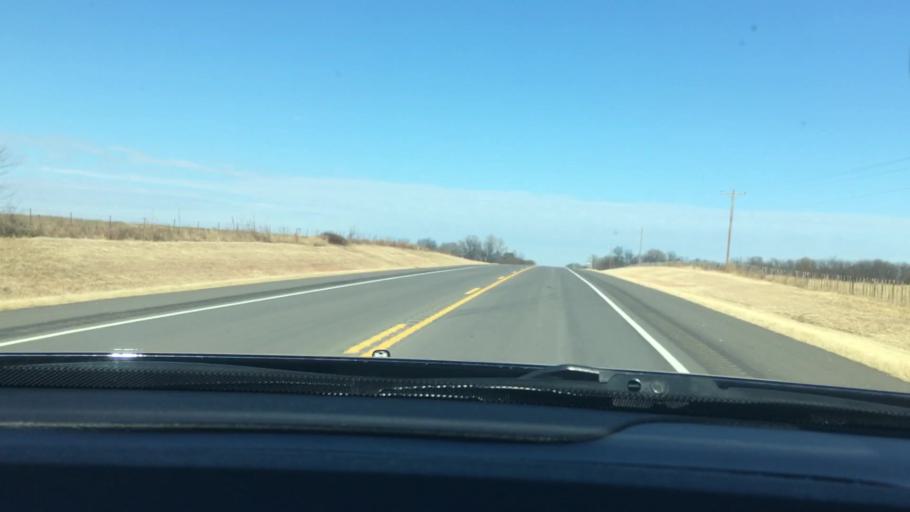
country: US
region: Oklahoma
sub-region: Murray County
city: Davis
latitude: 34.5535
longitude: -97.1332
